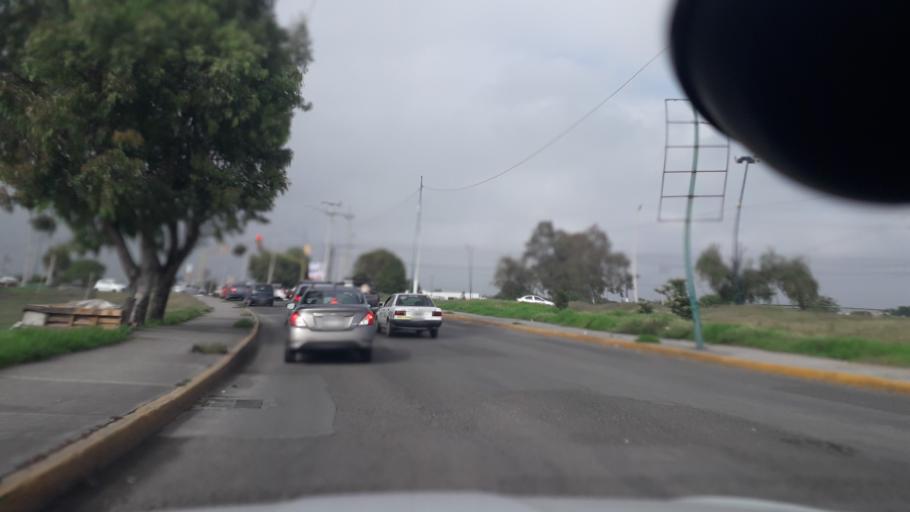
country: MX
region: Mexico
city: Coacalco
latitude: 19.6452
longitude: -99.1037
